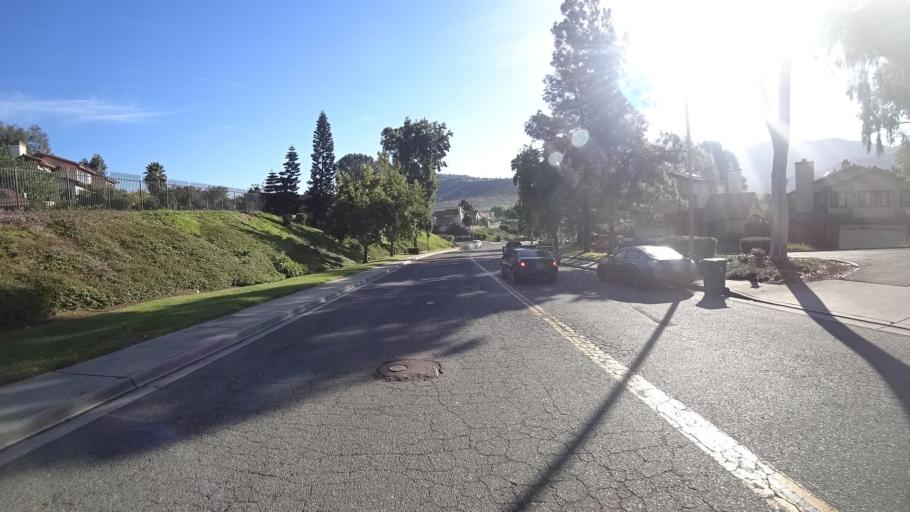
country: US
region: California
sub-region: San Diego County
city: La Presa
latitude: 32.7136
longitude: -116.9824
